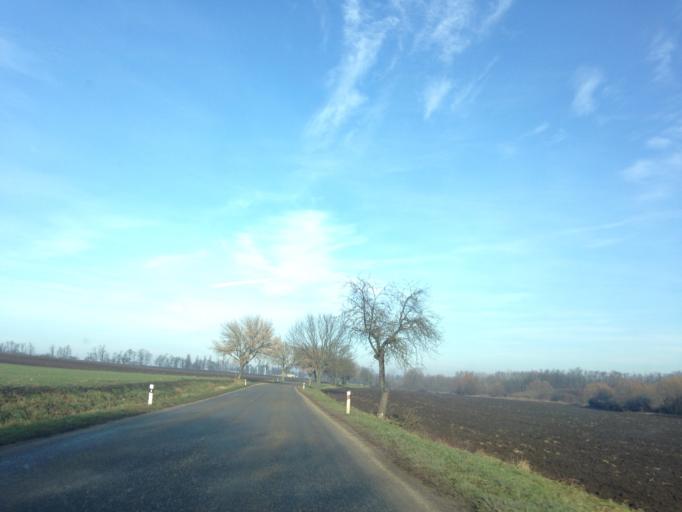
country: SK
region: Nitriansky
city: Svodin
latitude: 47.9714
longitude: 18.4075
